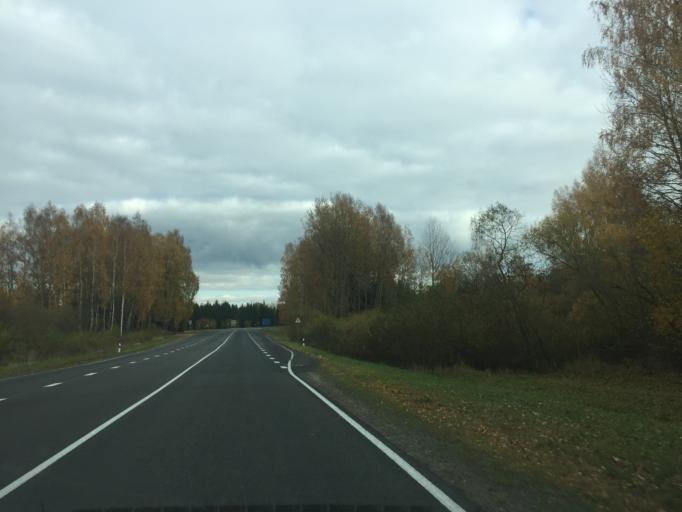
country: BY
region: Minsk
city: Svir
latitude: 54.8901
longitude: 26.3849
